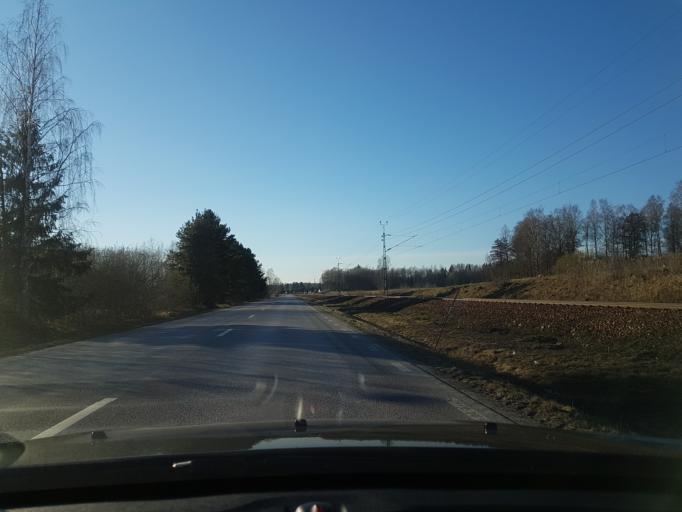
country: SE
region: Uppsala
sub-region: Heby Kommun
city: Morgongava
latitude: 59.9272
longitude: 16.9794
